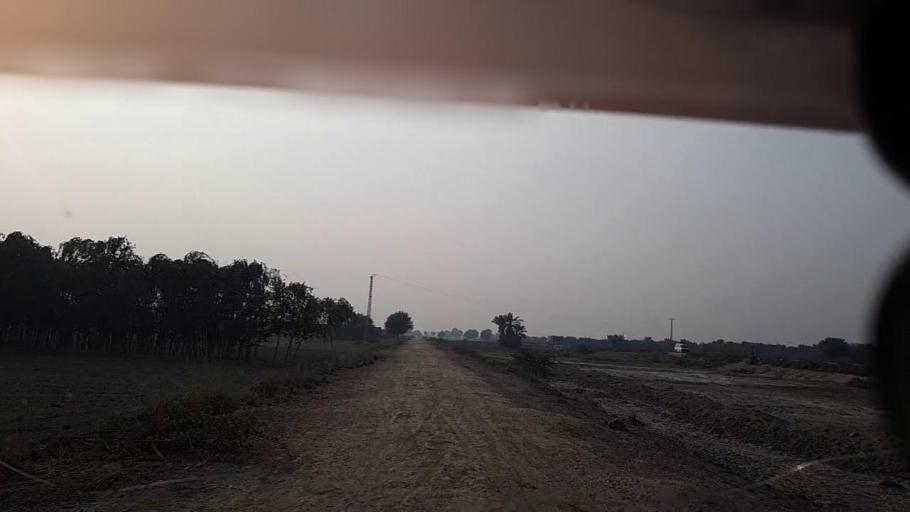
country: PK
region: Sindh
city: Gambat
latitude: 27.4355
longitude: 68.6078
